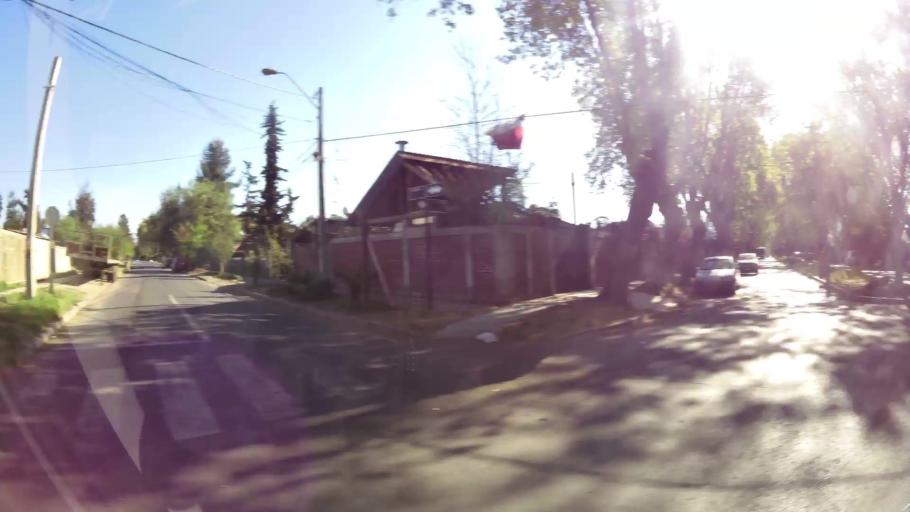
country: CL
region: Santiago Metropolitan
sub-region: Provincia de Talagante
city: Penaflor
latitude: -33.5983
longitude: -70.8769
